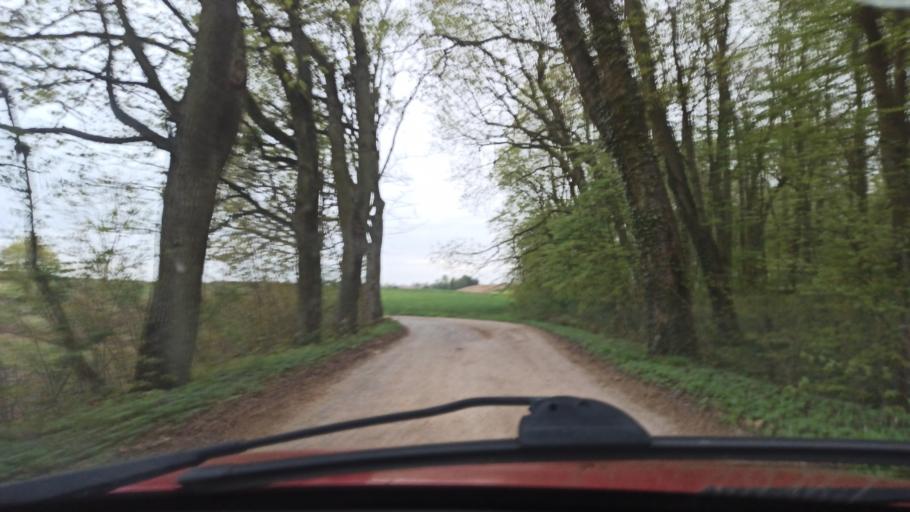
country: PL
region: Kujawsko-Pomorskie
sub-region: Powiat grudziadzki
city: Lasin
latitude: 53.5641
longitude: 19.0762
